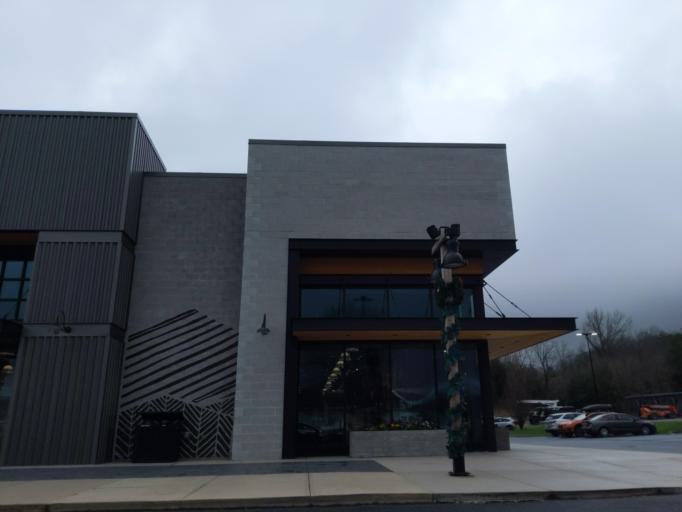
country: US
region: Tennessee
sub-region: Sevier County
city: Pigeon Forge
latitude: 35.8056
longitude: -83.5694
